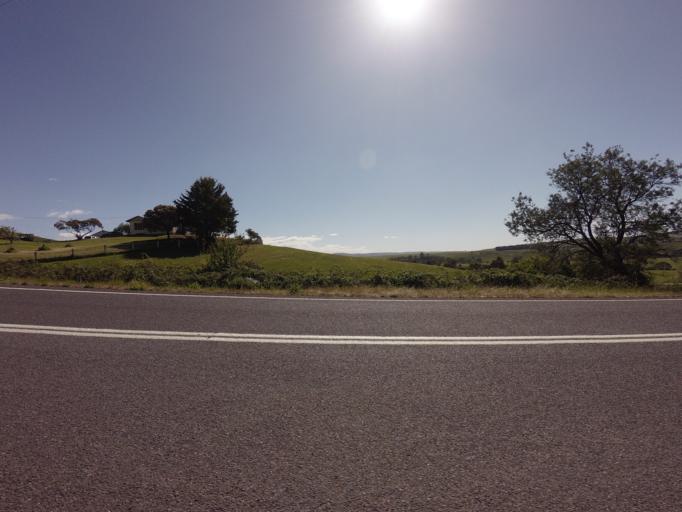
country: AU
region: Tasmania
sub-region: Derwent Valley
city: New Norfolk
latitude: -42.6946
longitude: 146.9390
